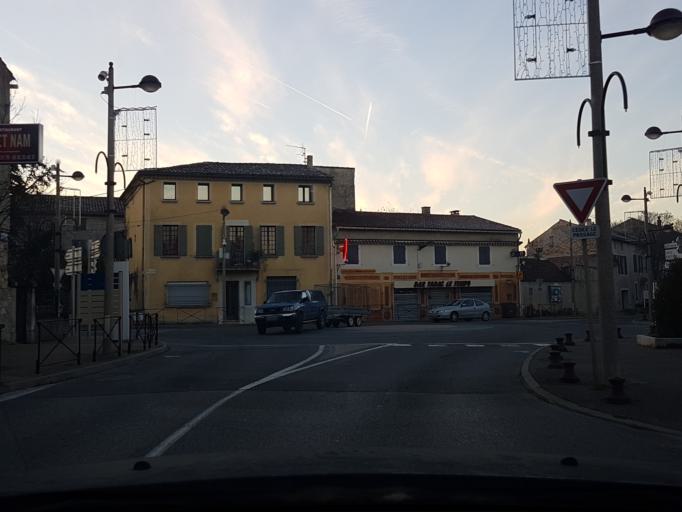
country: FR
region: Provence-Alpes-Cote d'Azur
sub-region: Departement du Vaucluse
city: Monteux
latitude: 44.0350
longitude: 4.9993
